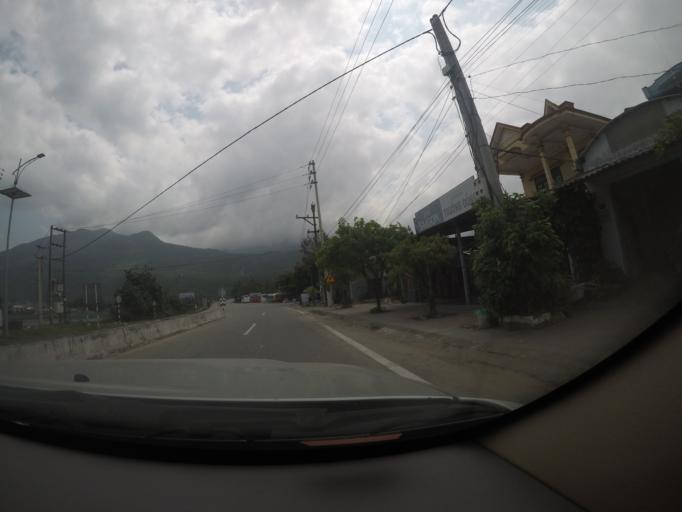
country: VN
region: Da Nang
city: Lien Chieu
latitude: 16.2292
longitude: 108.0832
